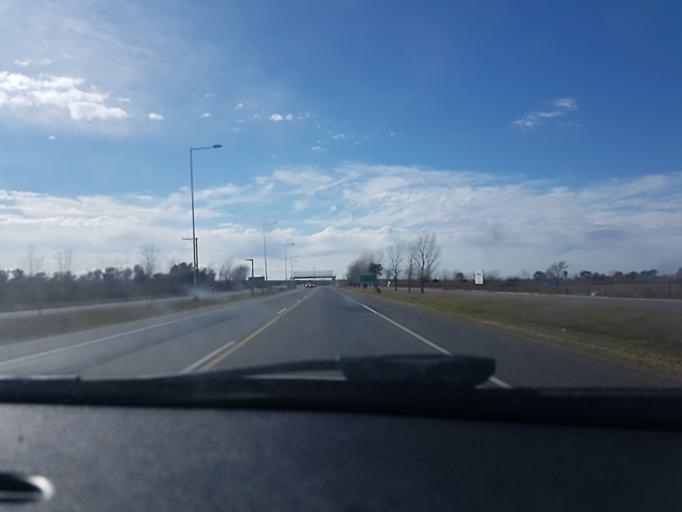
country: AR
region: Cordoba
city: Villa Allende
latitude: -31.3037
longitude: -64.2299
